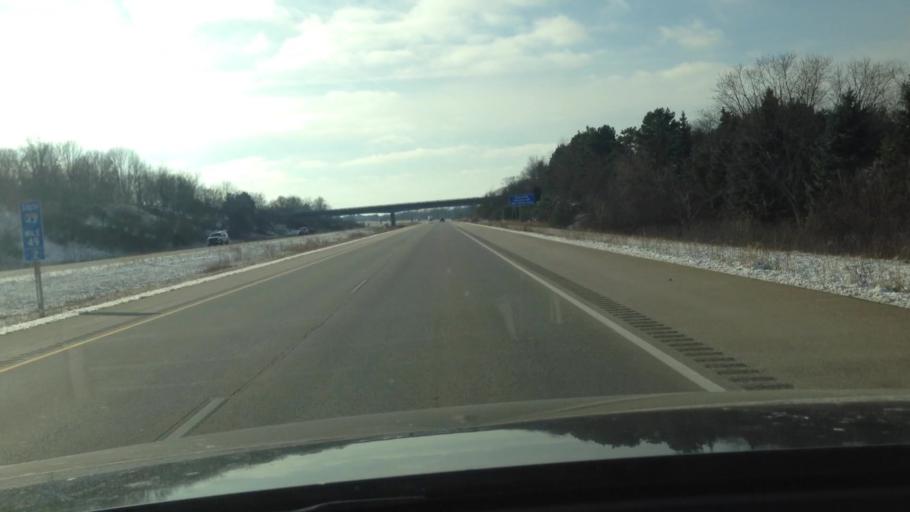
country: US
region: Wisconsin
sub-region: Waukesha County
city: Big Bend
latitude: 42.9034
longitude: -88.2445
